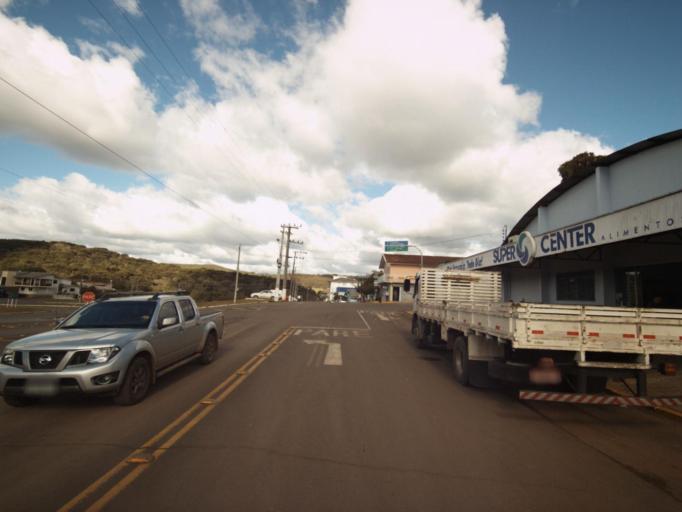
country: BR
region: Santa Catarina
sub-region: Joacaba
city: Joacaba
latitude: -27.0036
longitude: -51.7405
